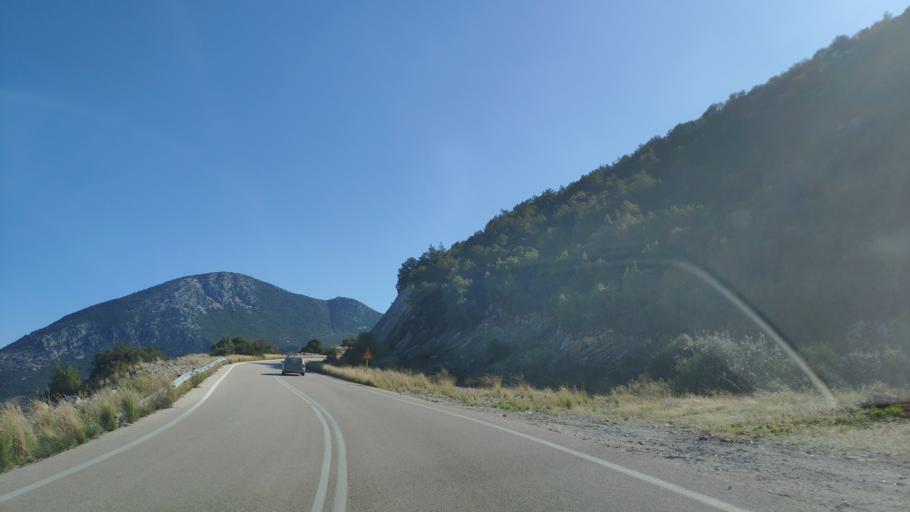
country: GR
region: Peloponnese
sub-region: Nomos Argolidos
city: Palaia Epidavros
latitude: 37.6193
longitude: 23.1479
